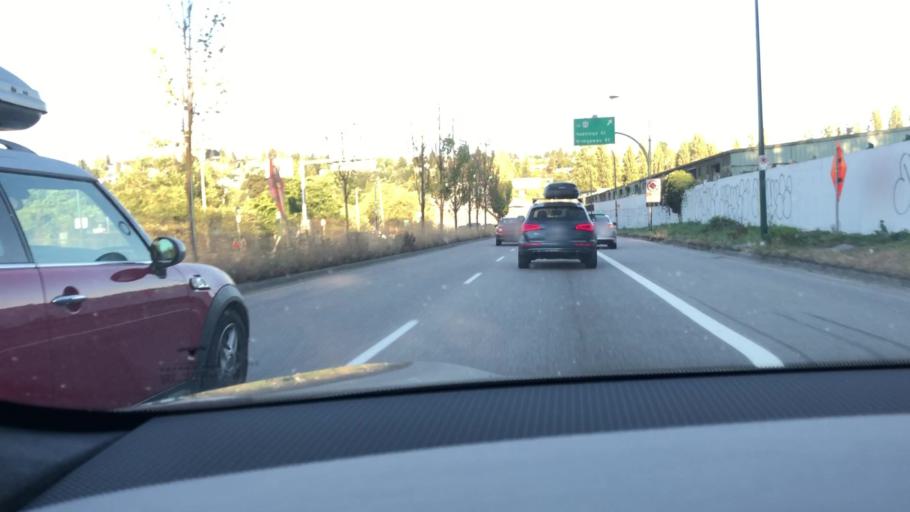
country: CA
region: British Columbia
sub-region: Fraser Valley Regional District
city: North Vancouver
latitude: 49.2885
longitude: -123.0388
